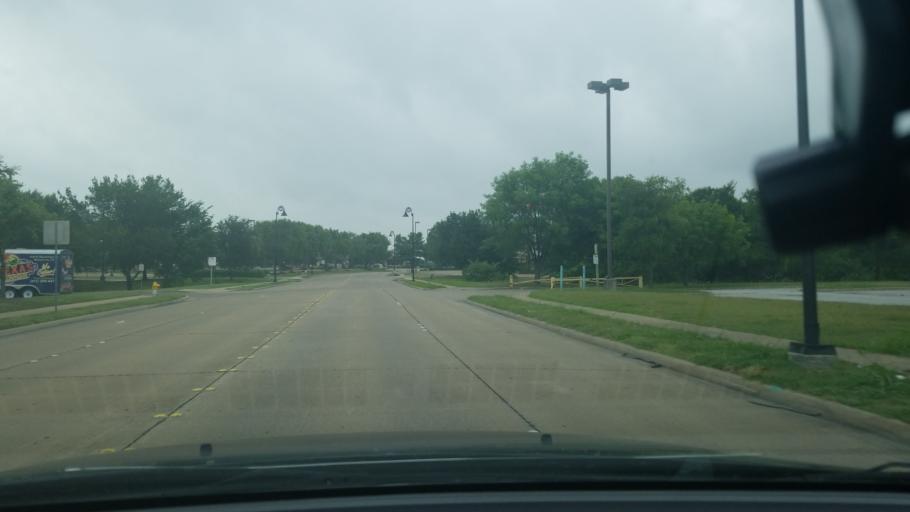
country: US
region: Texas
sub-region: Dallas County
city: Mesquite
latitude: 32.7858
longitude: -96.6261
